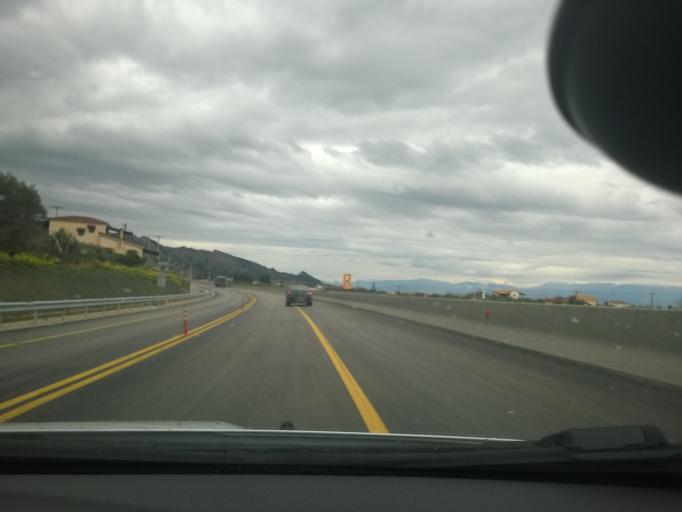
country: GR
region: Peloponnese
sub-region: Nomos Korinthias
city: Xylokastro
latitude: 38.0978
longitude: 22.5587
